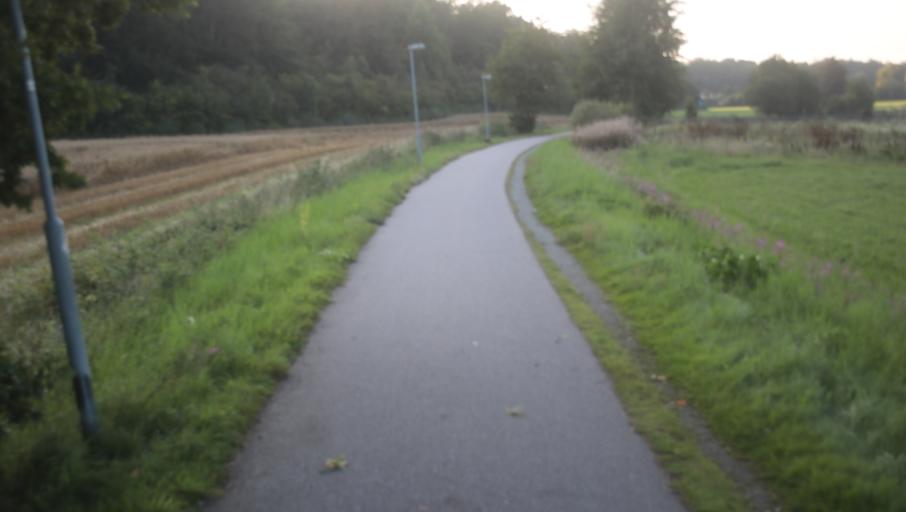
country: SE
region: Blekinge
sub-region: Karlshamns Kommun
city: Karlshamn
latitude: 56.1902
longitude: 14.8420
